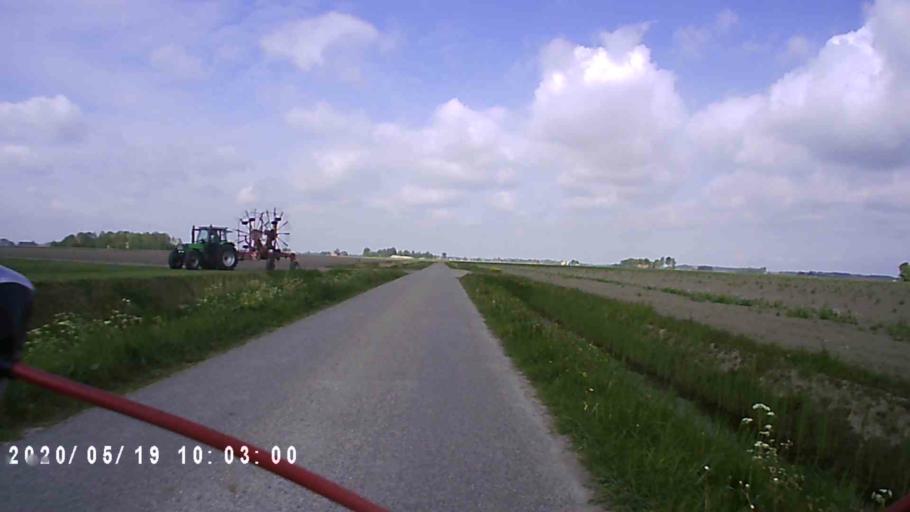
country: NL
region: Friesland
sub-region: Gemeente Kollumerland en Nieuwkruisland
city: Kollum
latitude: 53.3021
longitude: 6.2324
